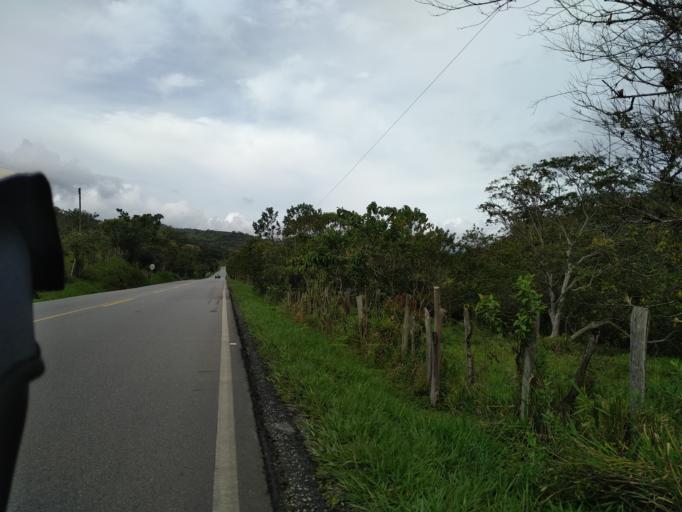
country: CO
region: Santander
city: Suaita
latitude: 6.1032
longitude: -73.3702
